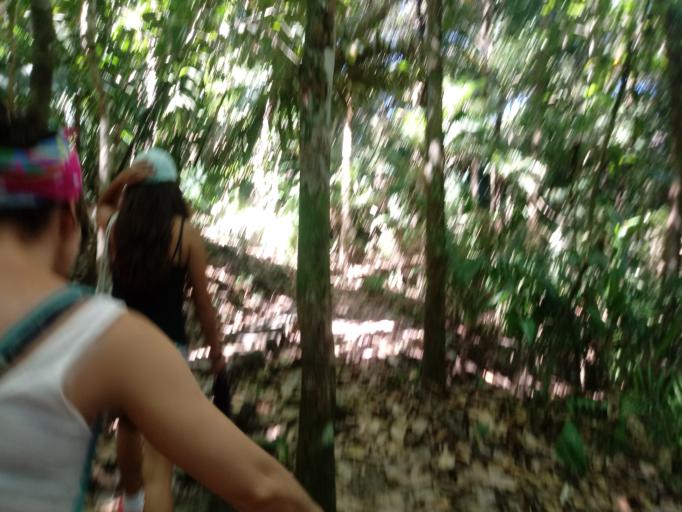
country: CR
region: Puntarenas
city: Paquera
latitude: 9.5863
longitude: -85.0949
